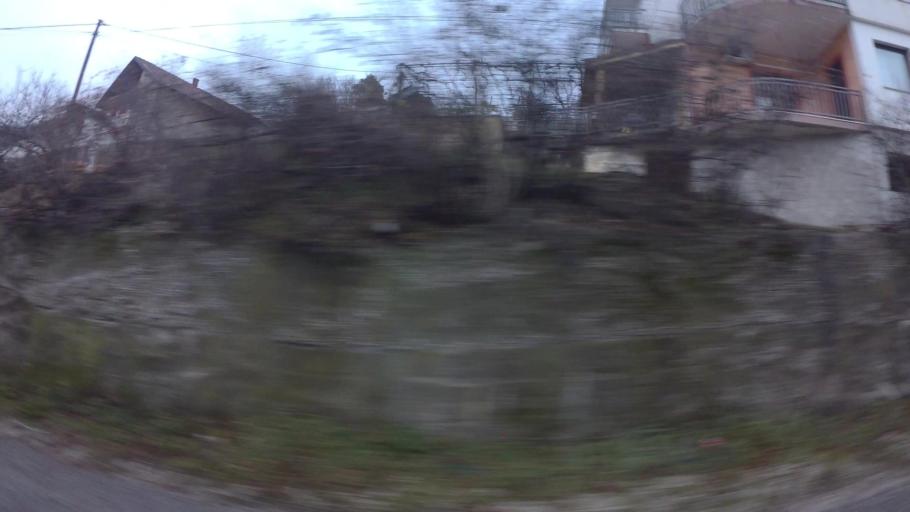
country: BA
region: Federation of Bosnia and Herzegovina
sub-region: Hercegovacko-Bosanski Kanton
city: Mostar
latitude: 43.3638
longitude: 17.8029
